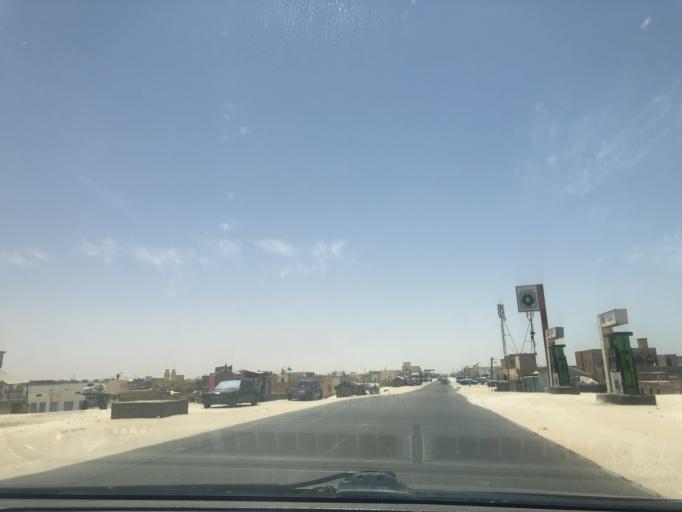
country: MR
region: Nouakchott
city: Nouakchott
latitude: 18.0187
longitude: -15.9587
